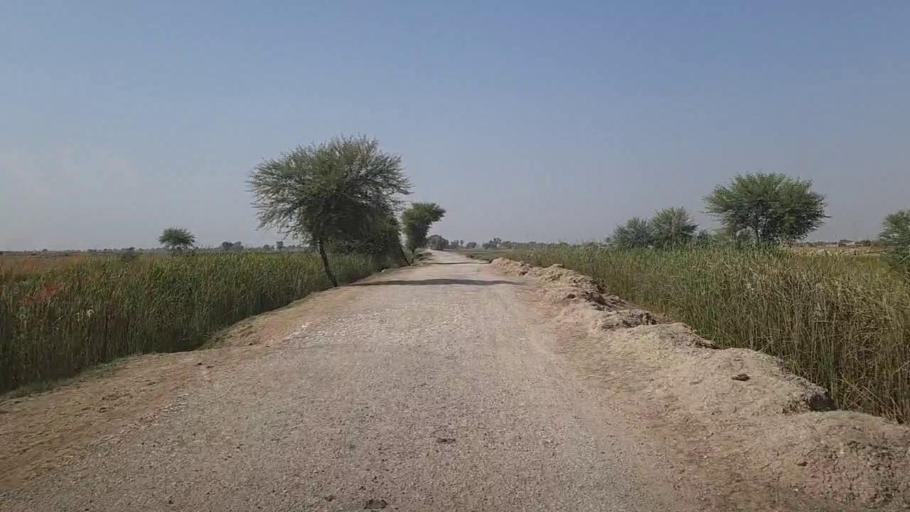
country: PK
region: Sindh
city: Kandhkot
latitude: 28.4012
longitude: 69.2627
